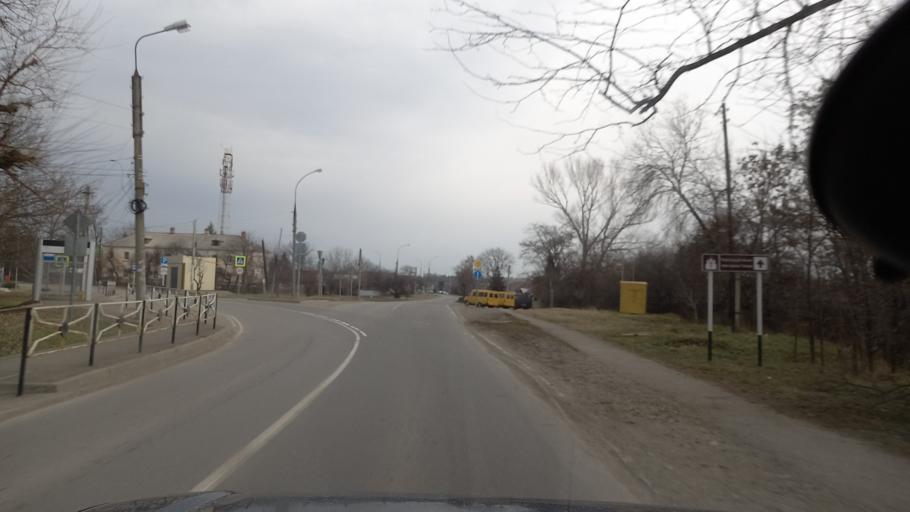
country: RU
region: Adygeya
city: Maykop
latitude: 44.5921
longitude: 40.1050
